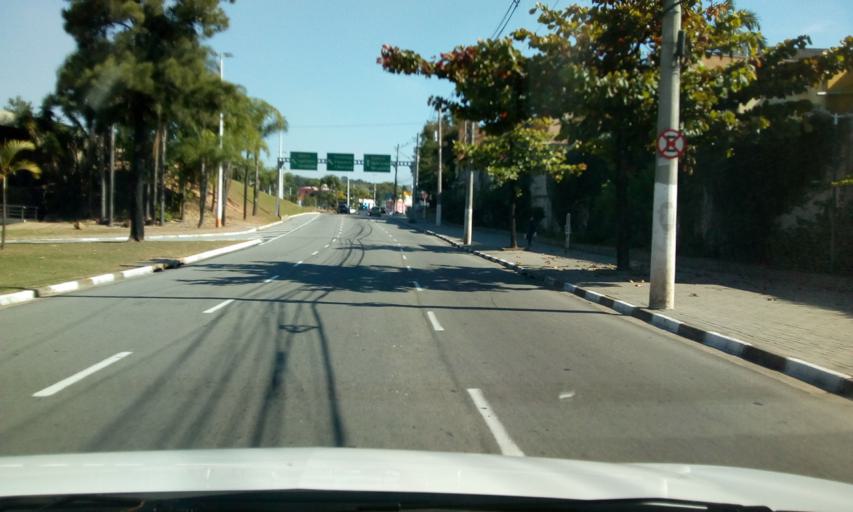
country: BR
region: Sao Paulo
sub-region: Barueri
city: Barueri
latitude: -23.5097
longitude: -46.8718
